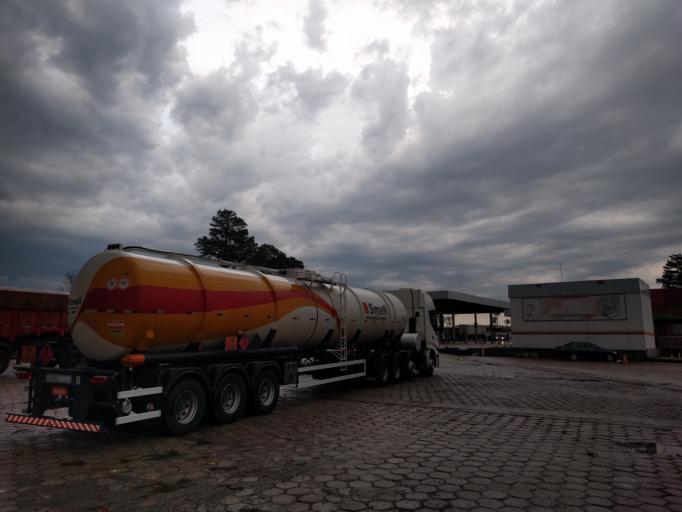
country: BR
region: Mato Grosso do Sul
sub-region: Bataipora
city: Bataipora
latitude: -21.7573
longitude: -53.2570
